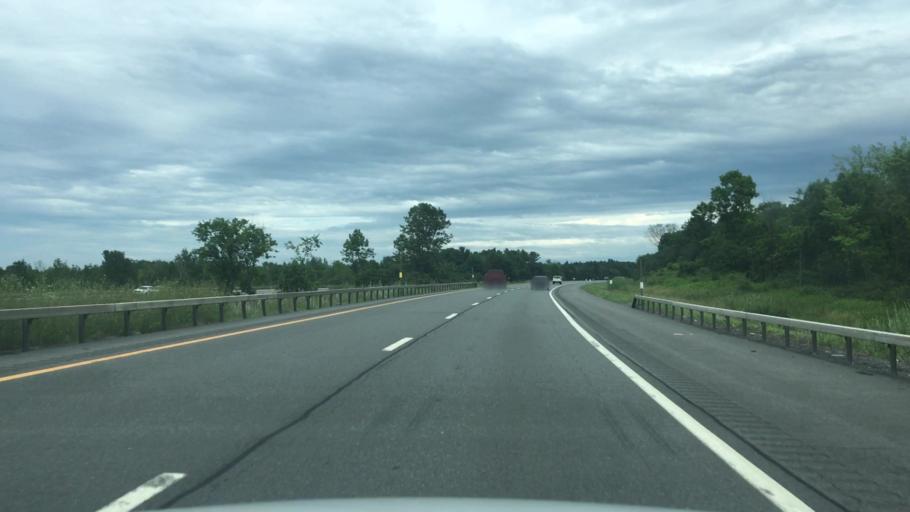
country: US
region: New York
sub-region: Schoharie County
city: Schoharie
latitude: 42.7231
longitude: -74.2409
